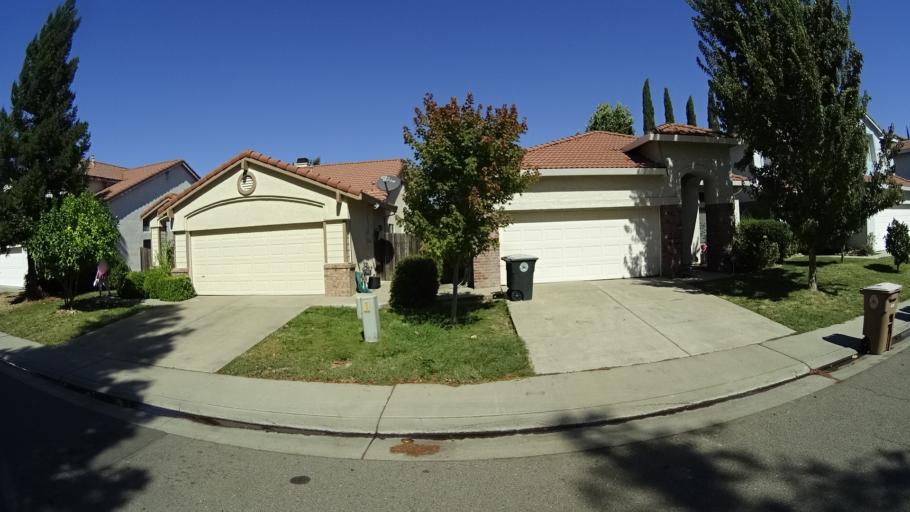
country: US
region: California
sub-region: Sacramento County
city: Laguna
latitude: 38.4247
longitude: -121.4237
